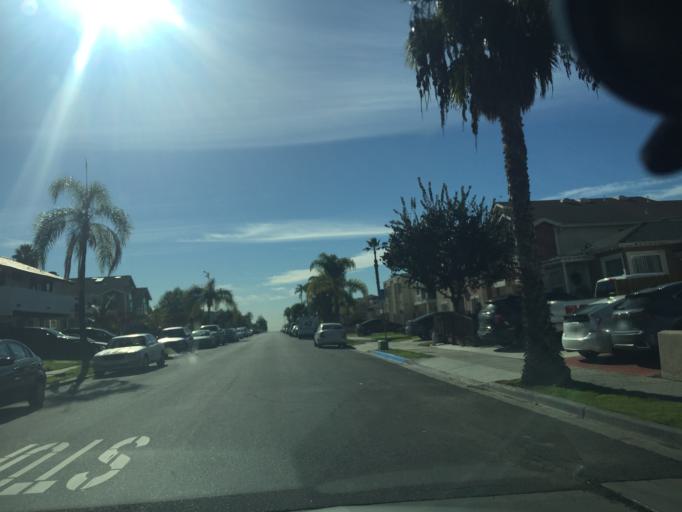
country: US
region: California
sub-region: San Diego County
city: Lemon Grove
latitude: 32.7590
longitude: -117.0869
